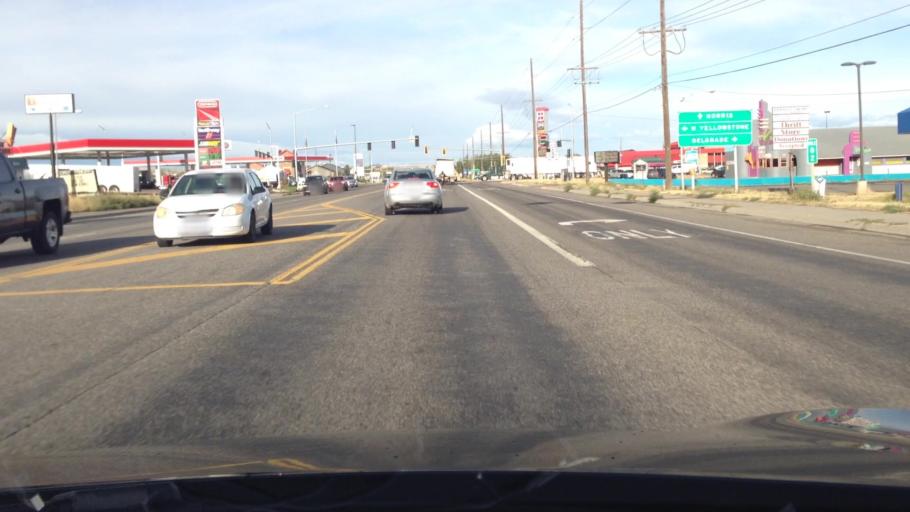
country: US
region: Montana
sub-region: Gallatin County
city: Four Corners
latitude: 45.6711
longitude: -111.1834
